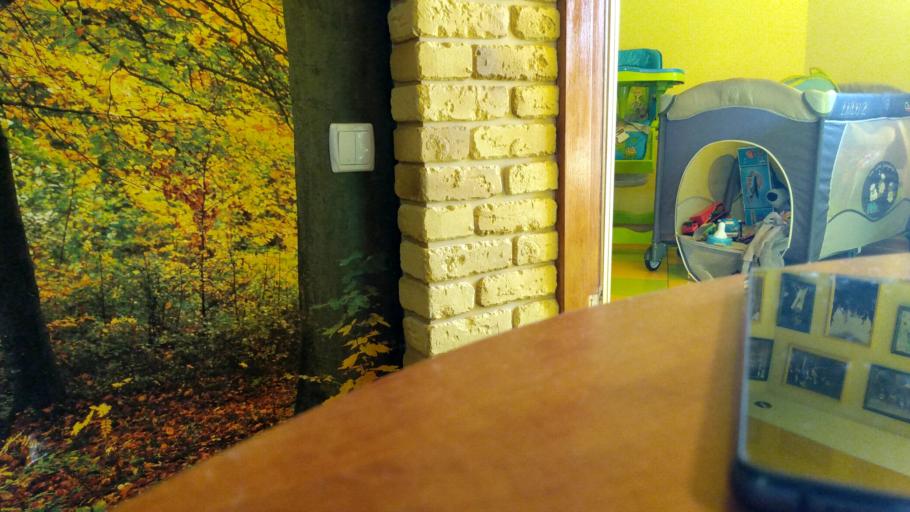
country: RU
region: Tverskaya
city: Likhoslavl'
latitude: 57.1716
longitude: 35.5699
